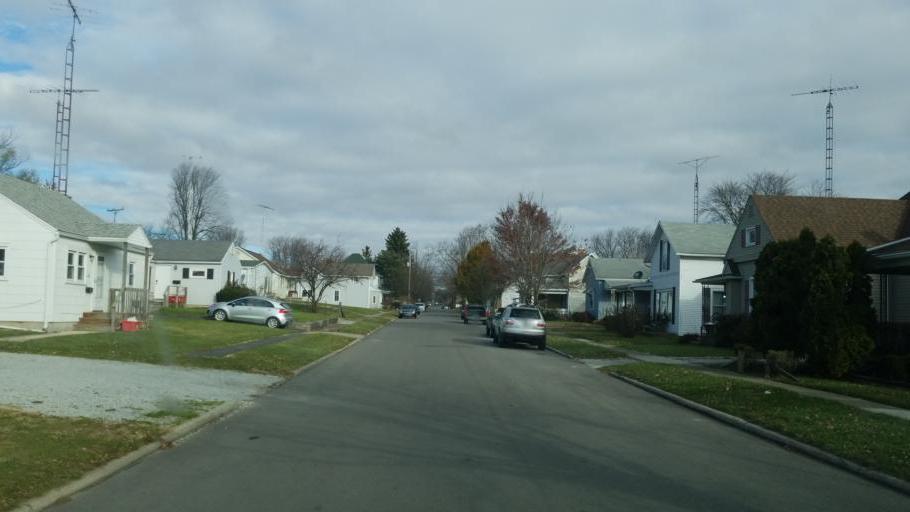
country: US
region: Ohio
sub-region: Hardin County
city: Kenton
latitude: 40.6441
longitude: -83.6046
